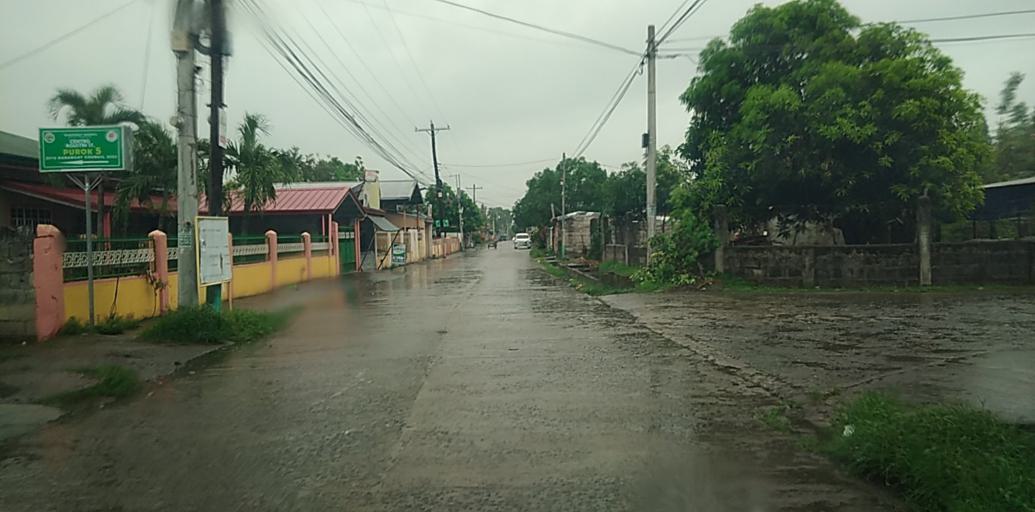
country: PH
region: Central Luzon
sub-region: Province of Pampanga
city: Arenas
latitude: 15.1713
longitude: 120.6845
